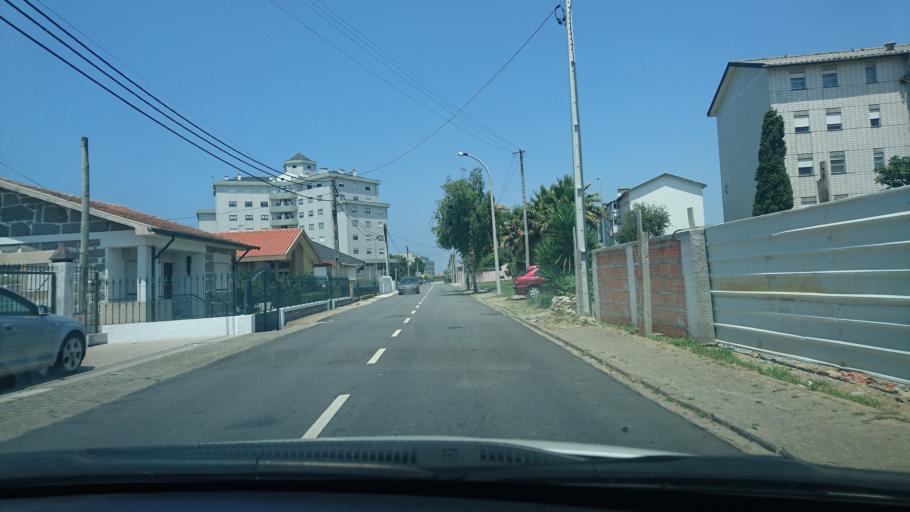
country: PT
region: Aveiro
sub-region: Ovar
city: Esmoriz
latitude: 40.9539
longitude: -8.6300
